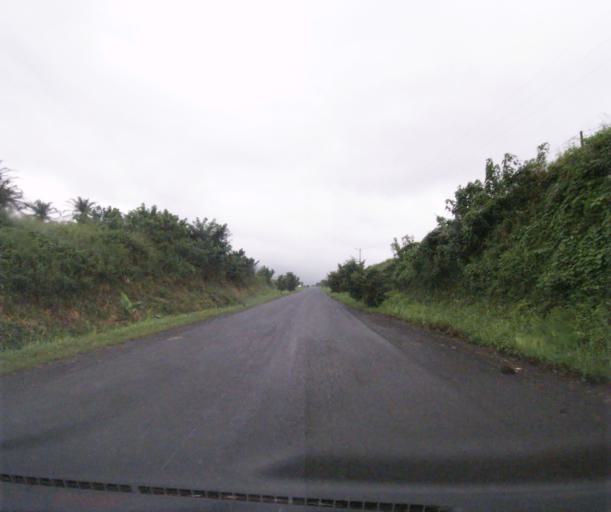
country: CM
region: South-West Province
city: Idenao
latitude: 4.2080
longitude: 8.9936
